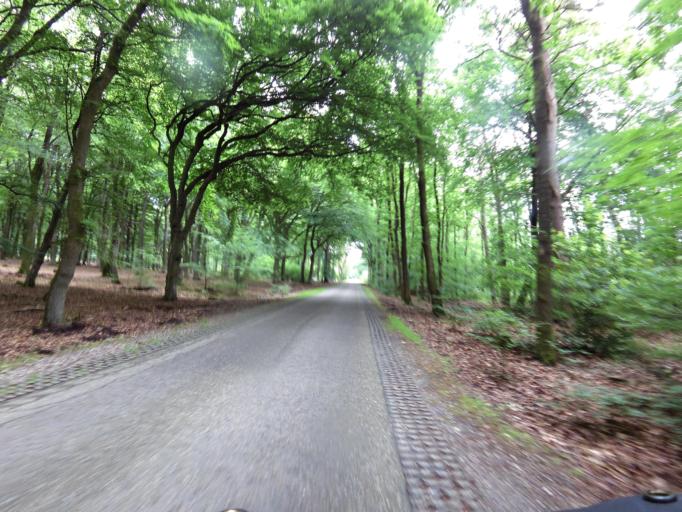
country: NL
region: Gelderland
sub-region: Gemeente Apeldoorn
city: Uddel
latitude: 52.2817
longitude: 5.8021
